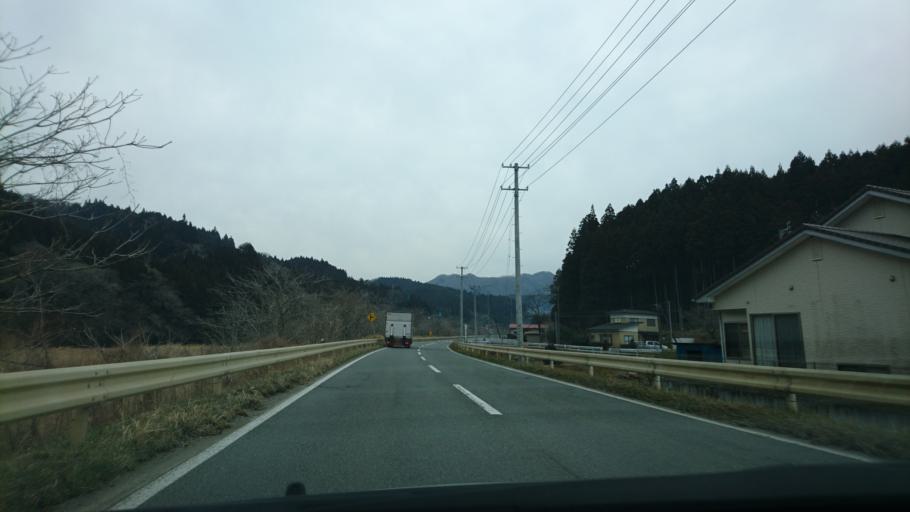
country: JP
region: Iwate
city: Ofunato
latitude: 39.0849
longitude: 141.5800
